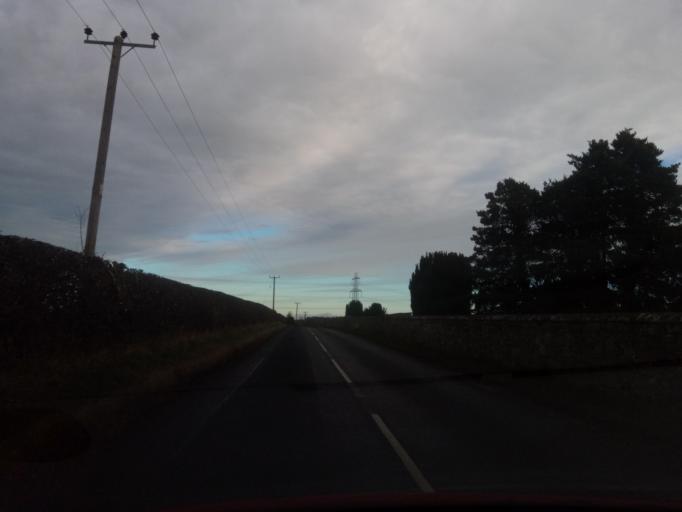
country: GB
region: Scotland
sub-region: The Scottish Borders
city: Coldstream
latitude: 55.6644
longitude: -2.2278
